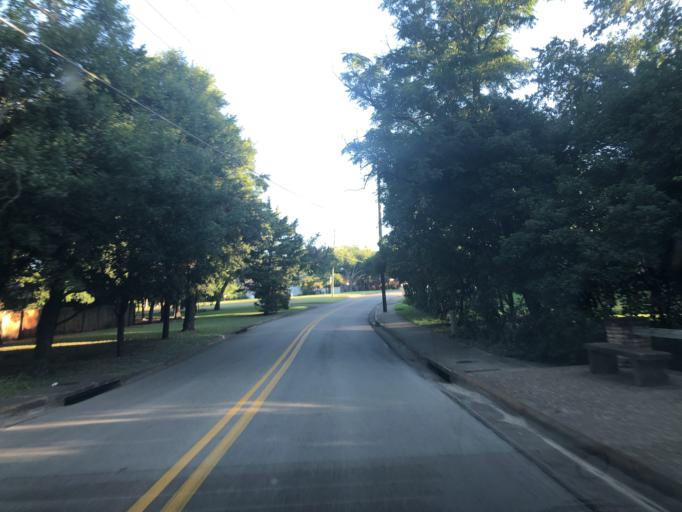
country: US
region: Texas
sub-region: Dallas County
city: Duncanville
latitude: 32.6372
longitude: -96.9348
